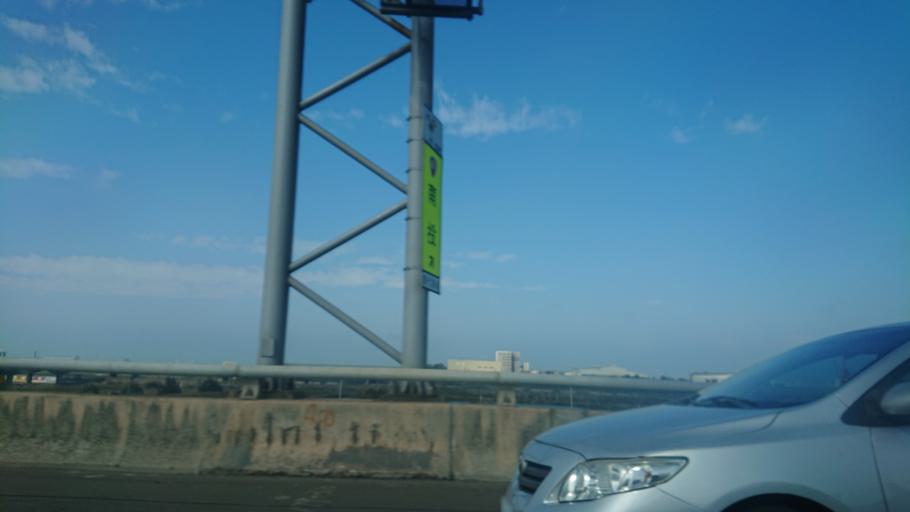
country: TW
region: Taiwan
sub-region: Changhua
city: Chang-hua
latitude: 24.0634
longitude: 120.4111
